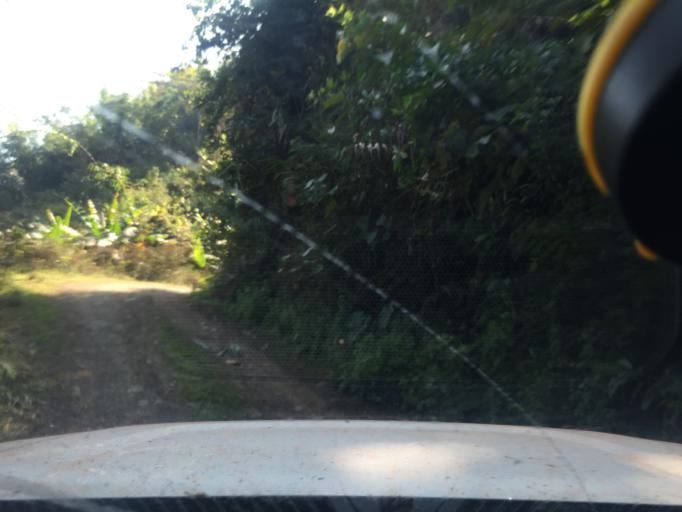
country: LA
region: Phongsali
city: Phongsali
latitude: 21.7042
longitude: 102.4010
